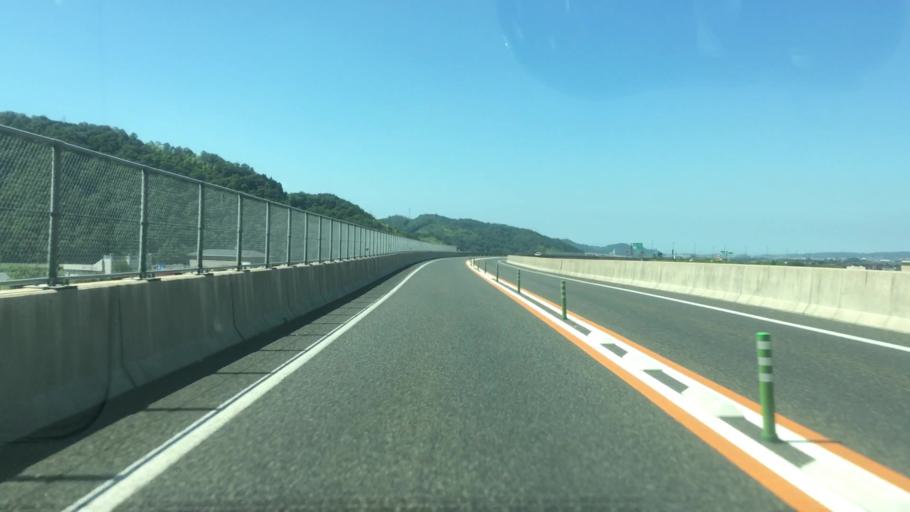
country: JP
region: Tottori
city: Tottori
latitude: 35.4166
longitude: 134.2061
